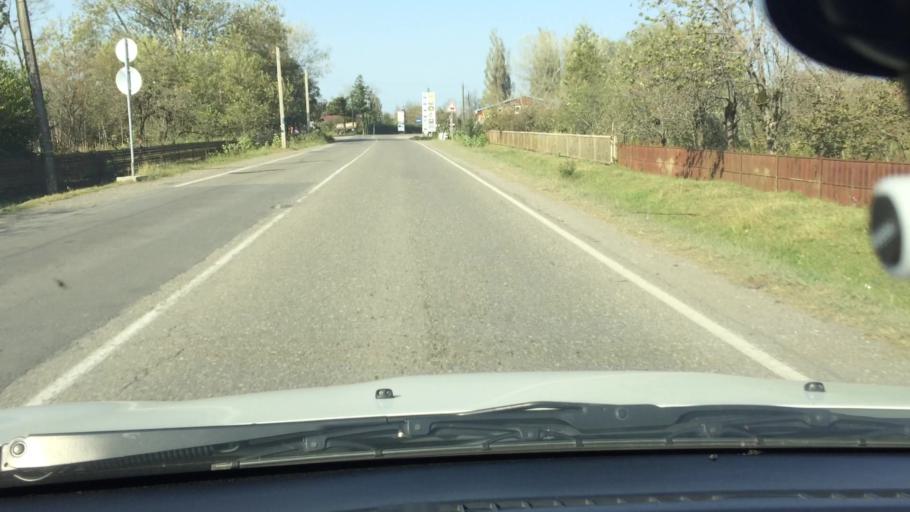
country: GE
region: Guria
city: Lanchkhuti
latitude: 42.0826
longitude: 41.9553
